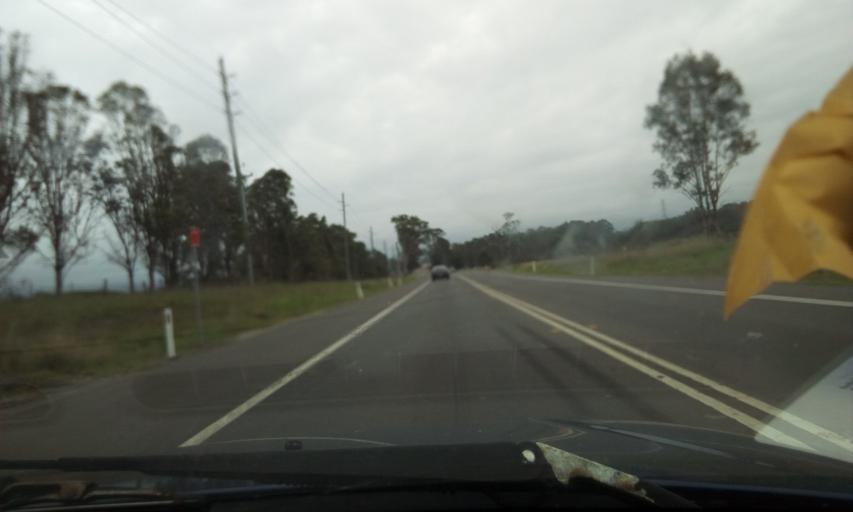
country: AU
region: New South Wales
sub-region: Penrith Municipality
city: Glenmore Park
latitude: -33.8029
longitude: 150.6969
